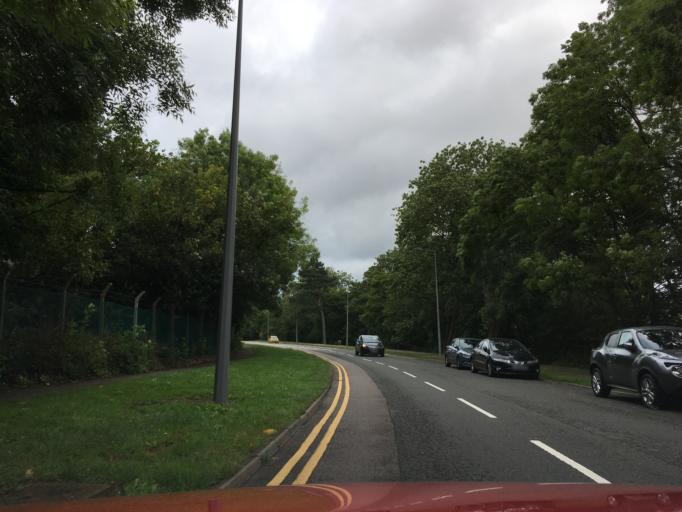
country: GB
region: England
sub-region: Buckinghamshire
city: Bletchley
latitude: 51.9985
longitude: -0.7382
